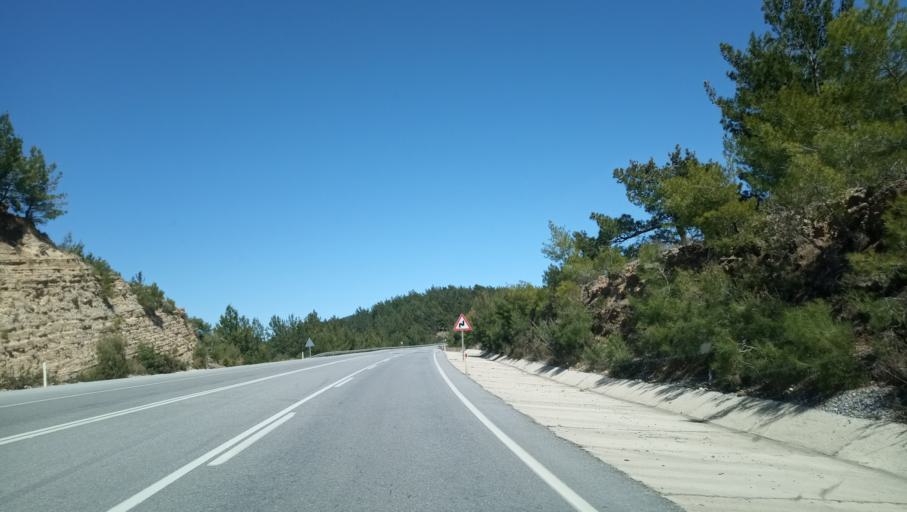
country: TR
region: Antalya
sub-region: Alanya
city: Okurcalar
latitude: 36.7770
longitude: 31.6852
